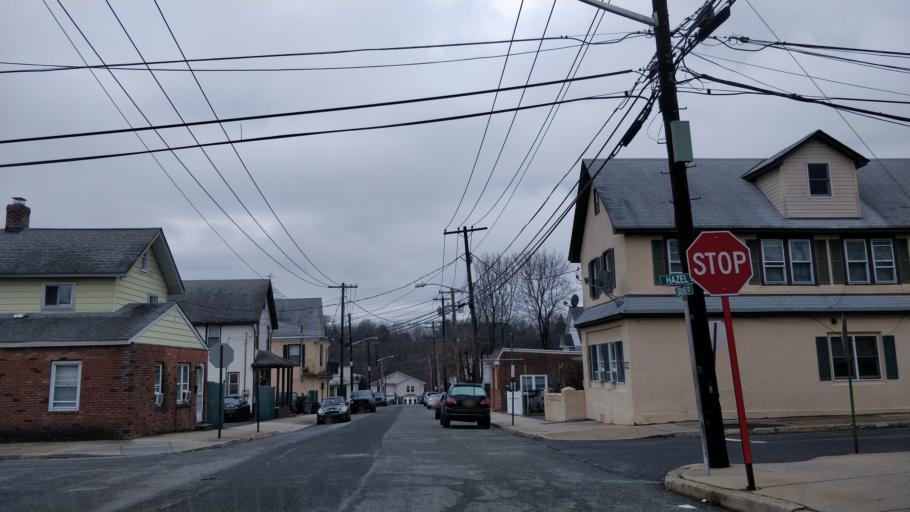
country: US
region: New York
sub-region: Nassau County
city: Glen Cove
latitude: 40.8562
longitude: -73.6212
